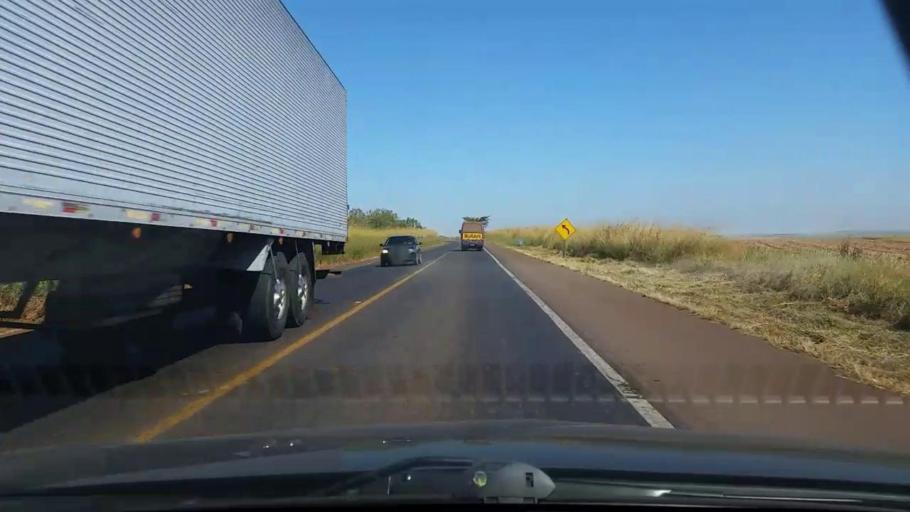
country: BR
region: Sao Paulo
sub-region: Igaracu Do Tiete
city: Igaracu do Tiete
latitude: -22.5606
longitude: -48.5627
